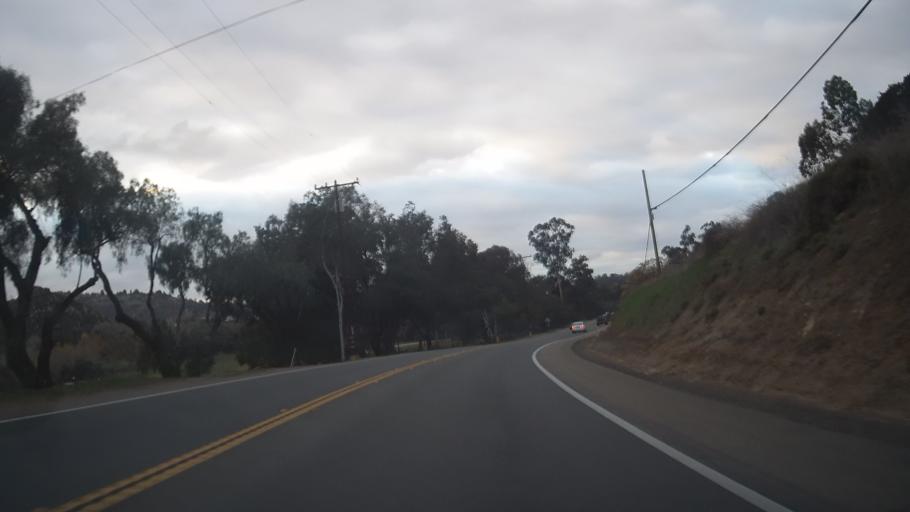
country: US
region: California
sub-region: San Diego County
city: Crest
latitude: 32.7793
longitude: -116.8692
